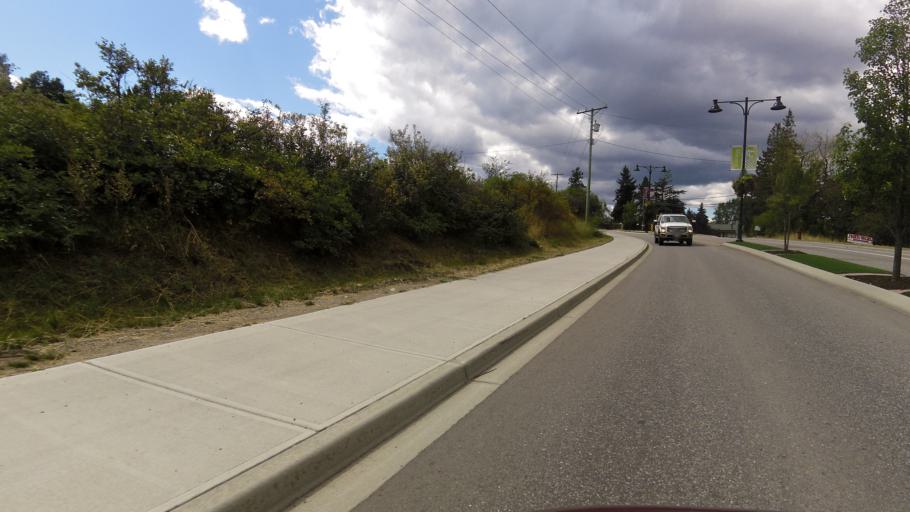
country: CA
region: British Columbia
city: West Kelowna
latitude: 49.8719
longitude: -119.5467
